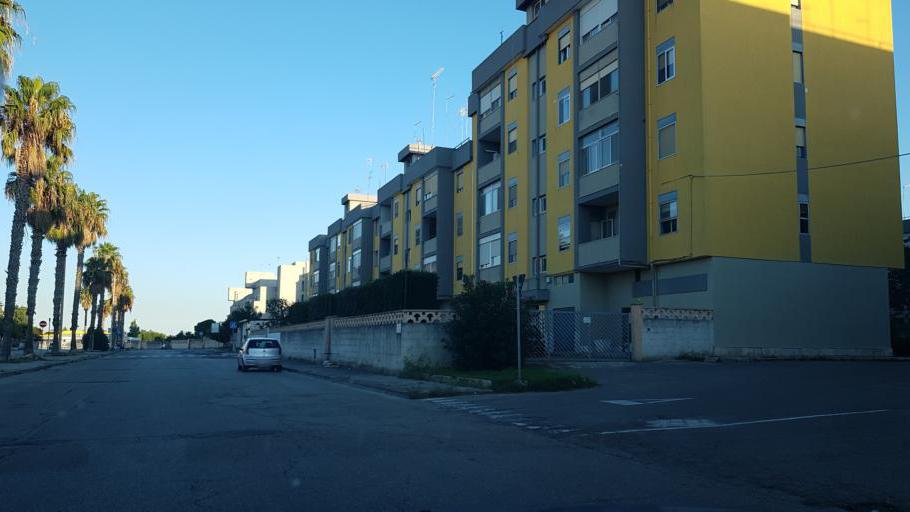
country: IT
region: Apulia
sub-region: Provincia di Brindisi
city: Brindisi
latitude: 40.6170
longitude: 17.9259
